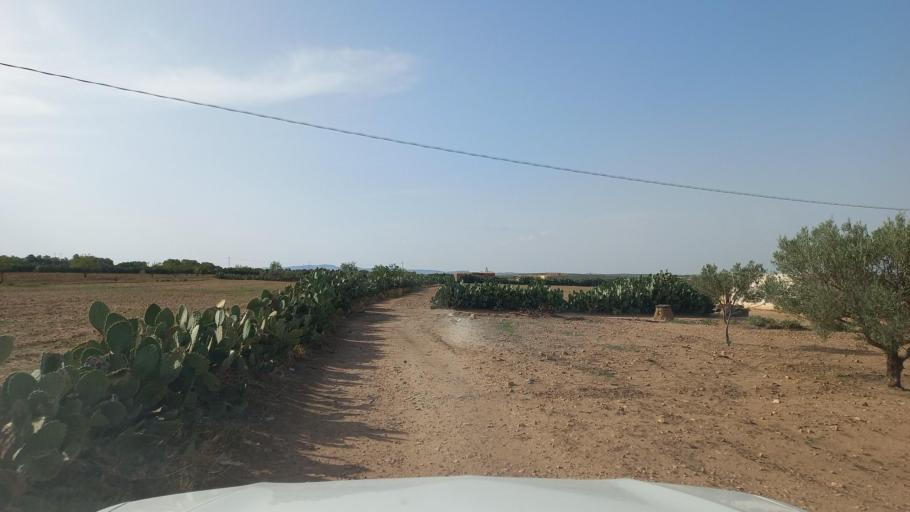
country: TN
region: Al Qasrayn
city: Kasserine
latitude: 35.3431
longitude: 8.8302
